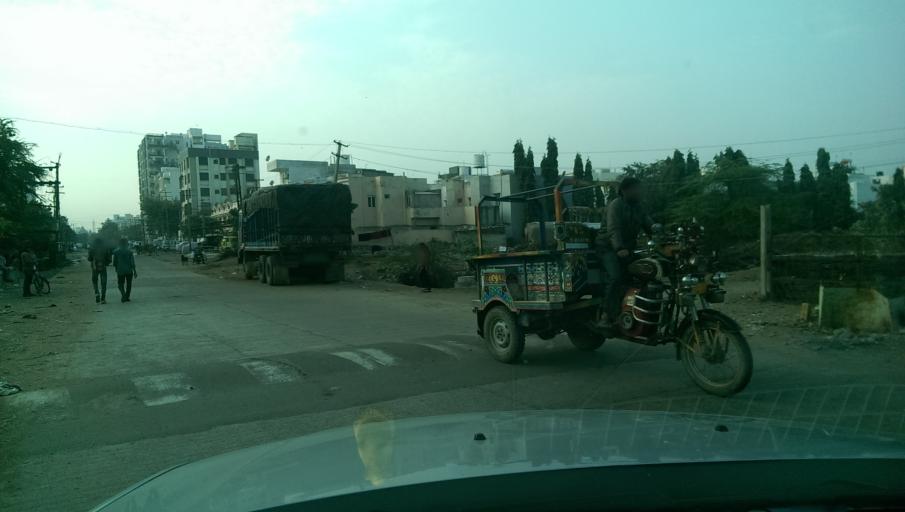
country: IN
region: Gujarat
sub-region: Jamnagar
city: Jamnagar
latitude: 22.4765
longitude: 70.0456
